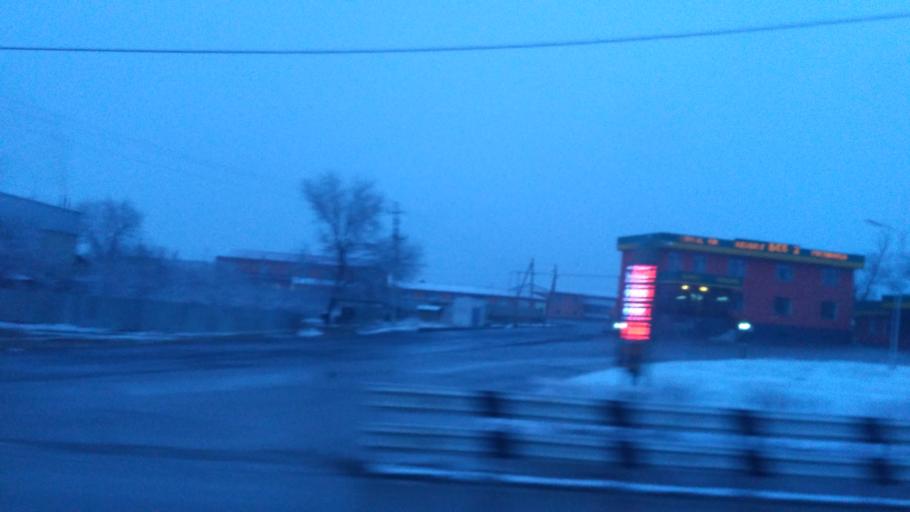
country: KZ
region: Ongtustik Qazaqstan
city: Shymkent
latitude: 42.3634
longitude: 69.5181
